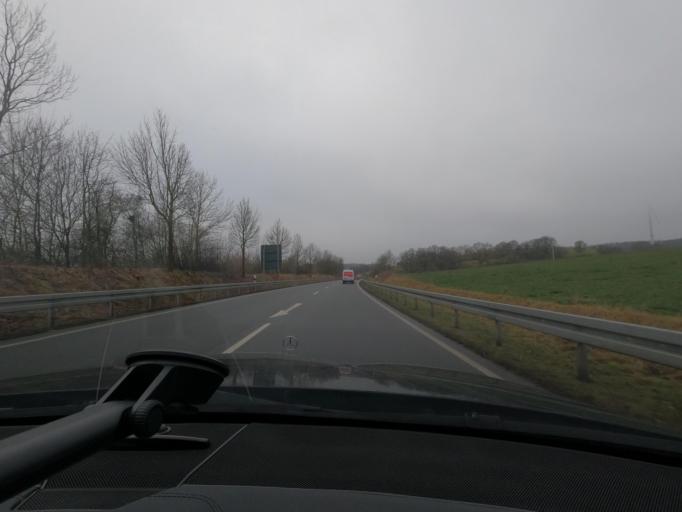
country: DE
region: Hesse
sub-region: Regierungsbezirk Kassel
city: Bad Arolsen
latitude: 51.3937
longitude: 9.0063
